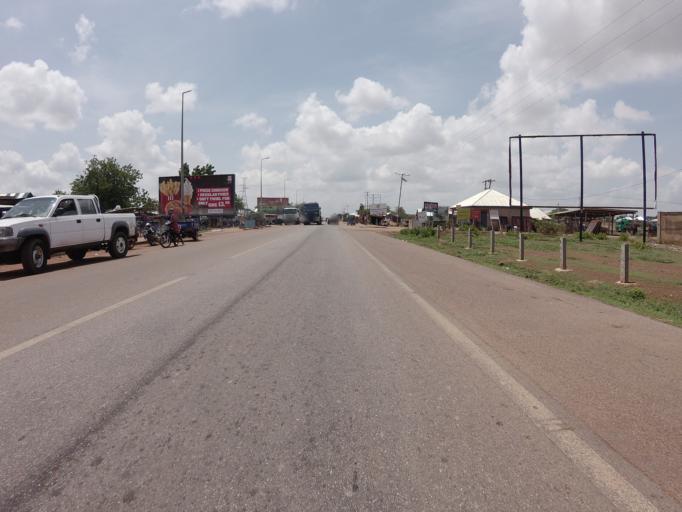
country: GH
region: Northern
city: Tamale
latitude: 9.3753
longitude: -0.8724
